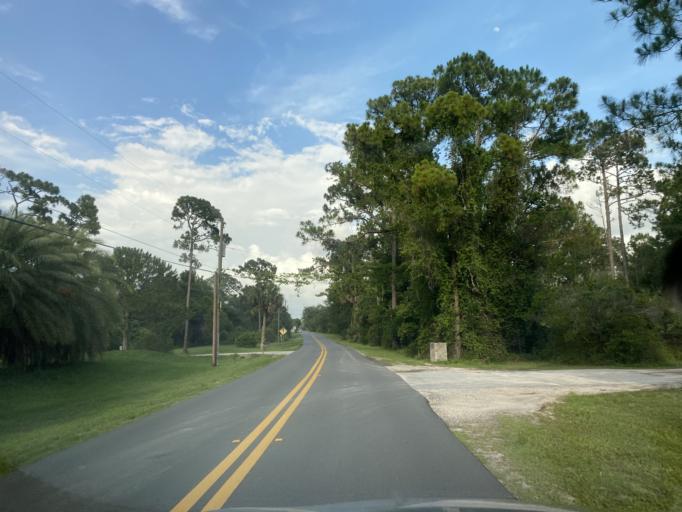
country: US
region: Florida
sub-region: Seminole County
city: Midway
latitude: 28.8455
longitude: -81.1921
